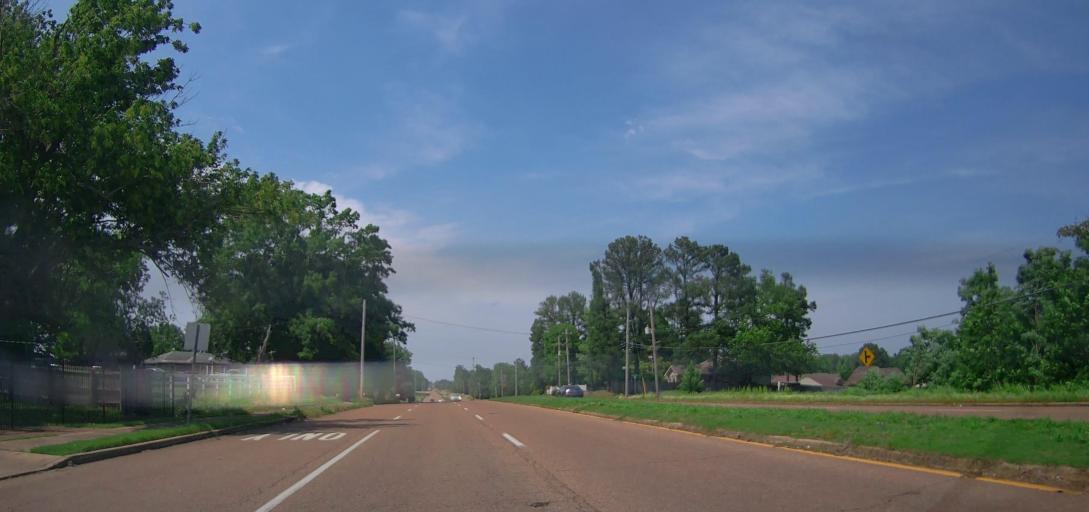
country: US
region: Mississippi
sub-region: De Soto County
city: Olive Branch
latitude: 34.9965
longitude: -89.8309
